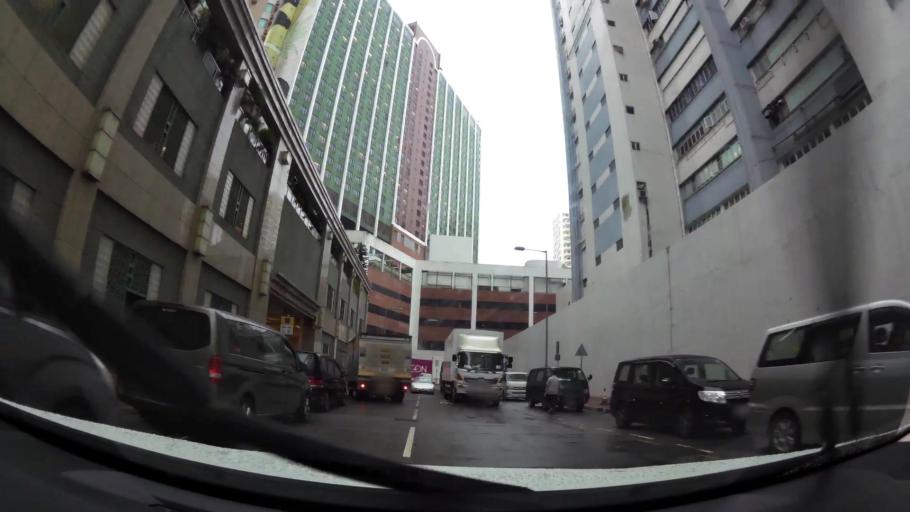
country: HK
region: Tsuen Wan
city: Tsuen Wan
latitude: 22.3683
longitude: 114.1203
